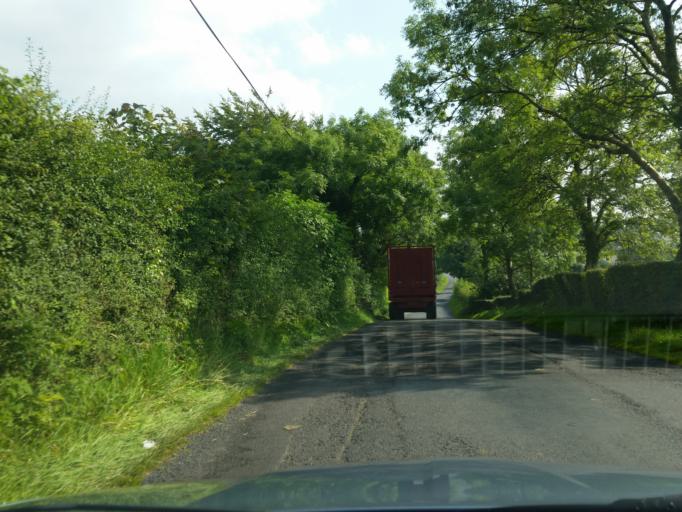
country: GB
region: Northern Ireland
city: Ballinamallard
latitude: 54.3381
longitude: -7.5373
